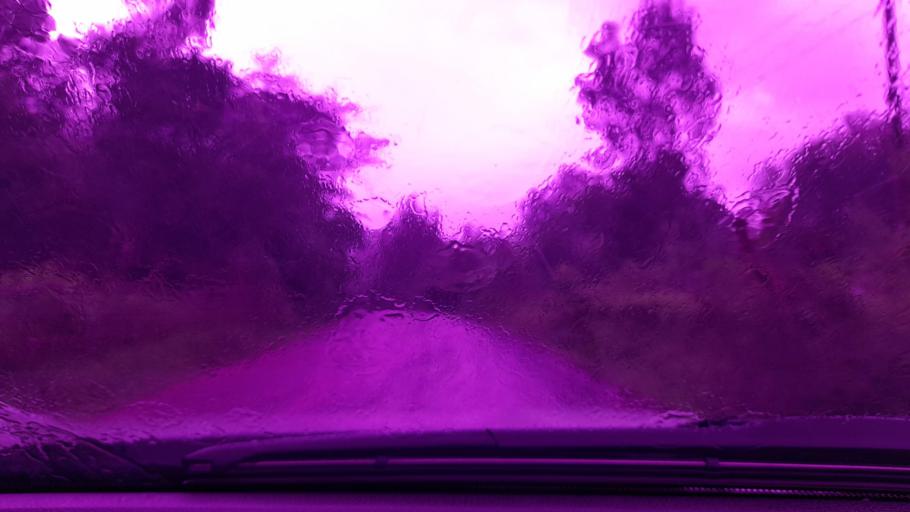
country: ET
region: Oromiya
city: Metu
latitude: 8.3747
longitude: 35.6003
